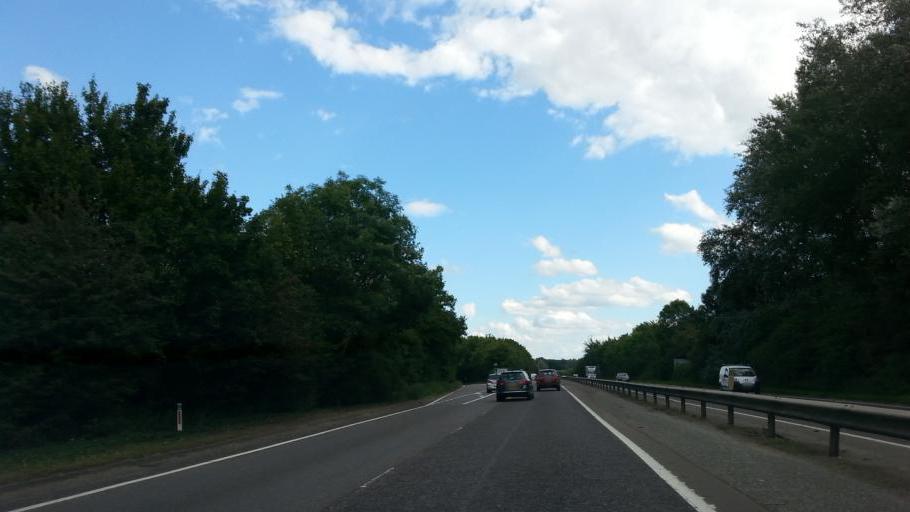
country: GB
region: England
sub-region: Suffolk
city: Woolpit
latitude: 52.2271
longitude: 0.9003
